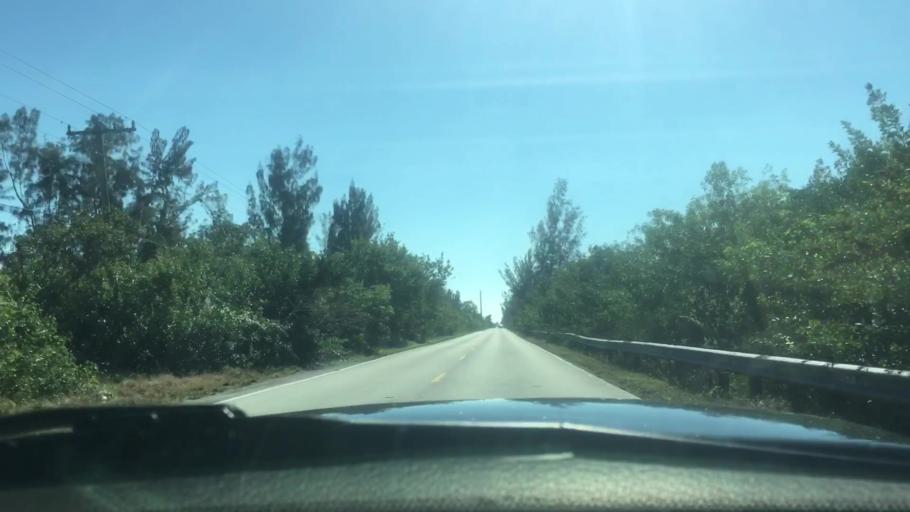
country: US
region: Florida
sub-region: Miami-Dade County
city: Florida City
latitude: 25.3671
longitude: -80.4299
